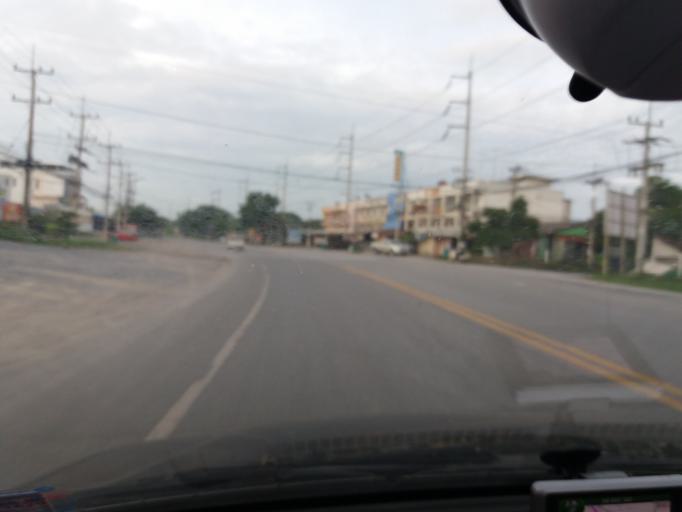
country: TH
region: Suphan Buri
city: U Thong
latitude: 14.4040
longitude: 99.8967
